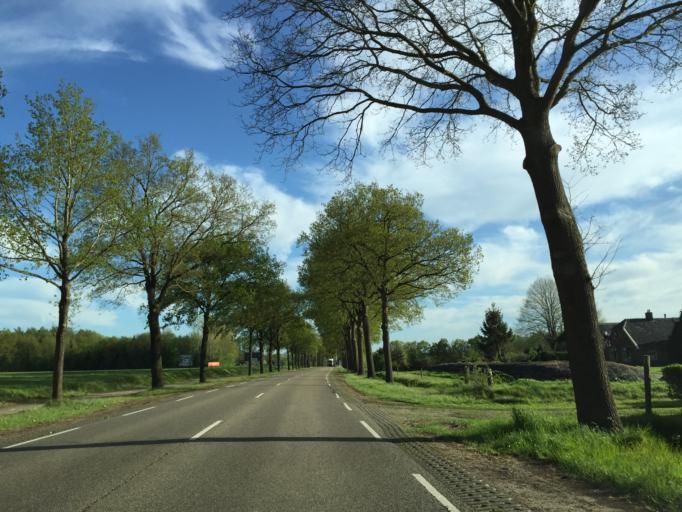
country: NL
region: Overijssel
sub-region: Gemeente Dalfsen
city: Dalfsen
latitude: 52.5245
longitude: 6.2606
